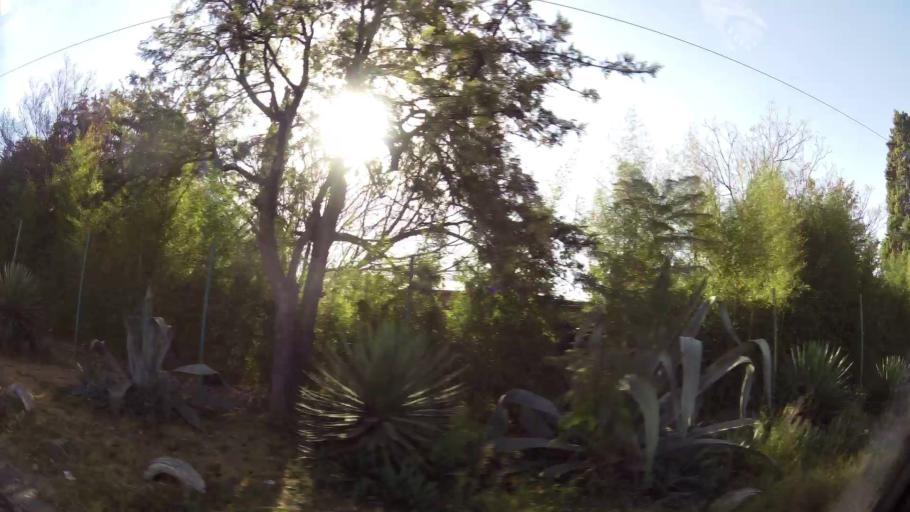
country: ZA
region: Gauteng
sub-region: City of Johannesburg Metropolitan Municipality
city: Diepsloot
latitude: -26.0242
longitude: 27.9724
